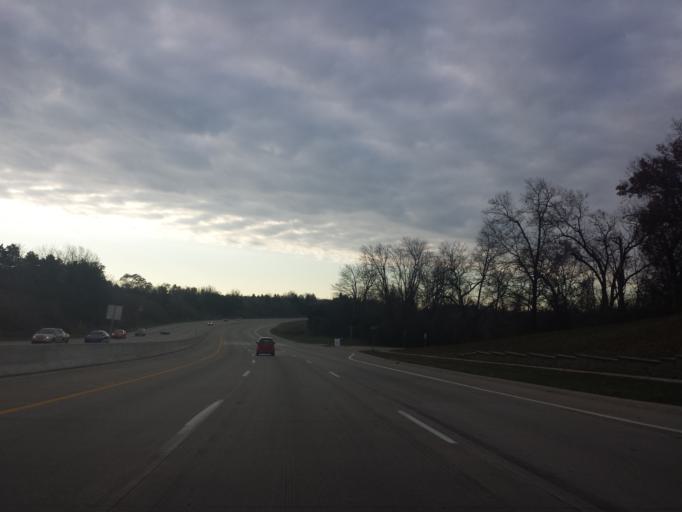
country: US
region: Michigan
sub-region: Oakland County
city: Bloomfield Hills
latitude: 42.5762
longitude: -83.2809
